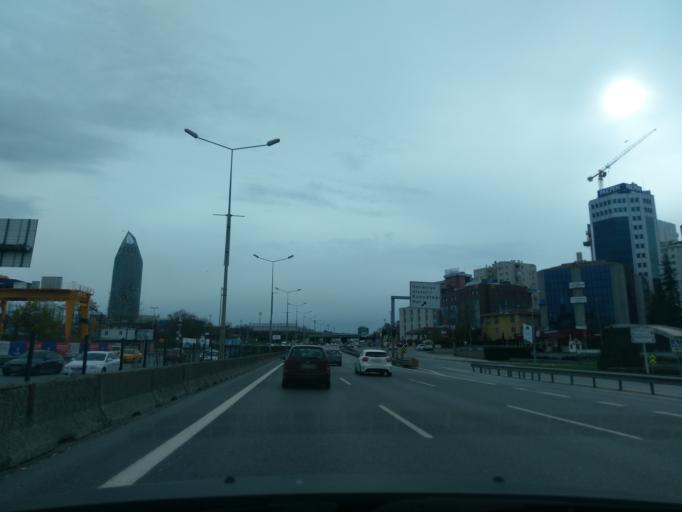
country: TR
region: Istanbul
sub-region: Atasehir
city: Atasehir
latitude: 40.9850
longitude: 29.0908
